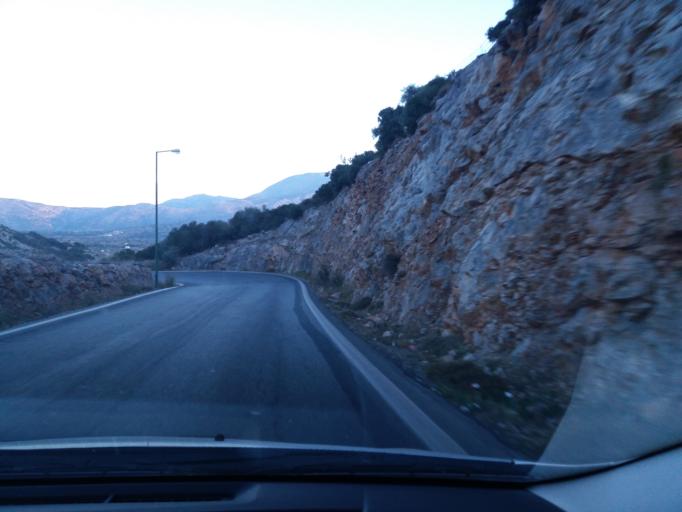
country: GR
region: Crete
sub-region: Nomos Irakleiou
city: Mokhos
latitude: 35.2022
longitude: 25.4565
